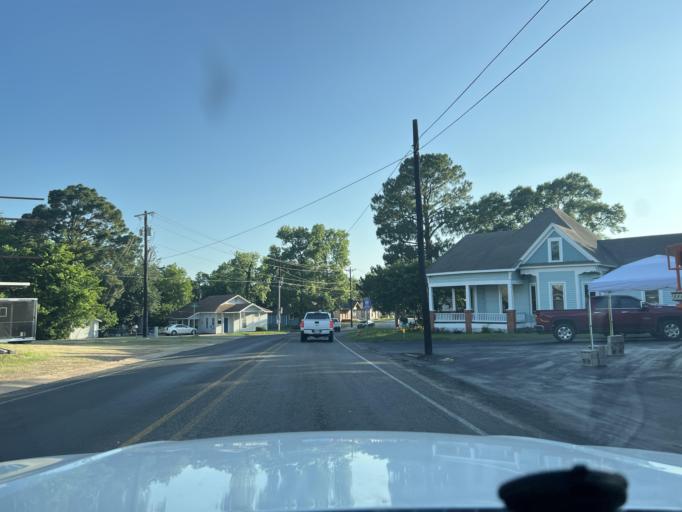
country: US
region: Texas
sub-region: Washington County
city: Brenham
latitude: 30.1731
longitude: -96.3905
